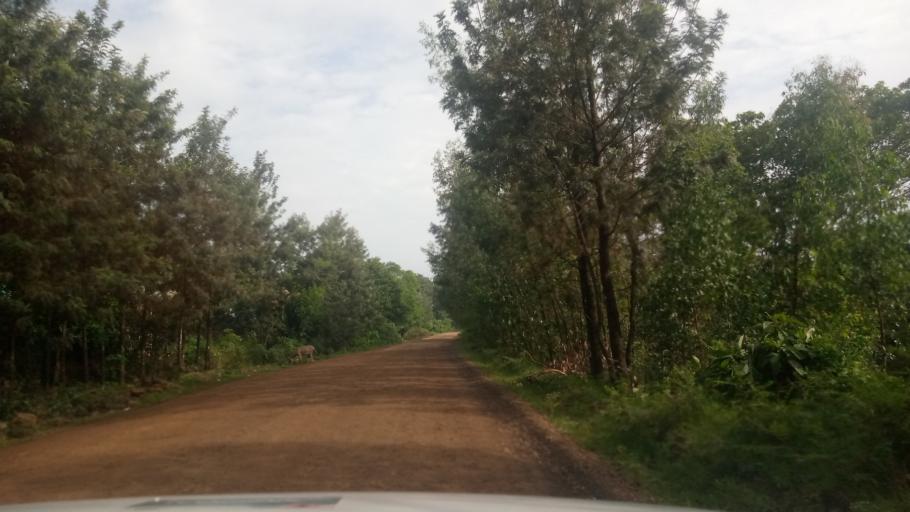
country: ET
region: Oromiya
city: Agaro
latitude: 7.8440
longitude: 36.6590
